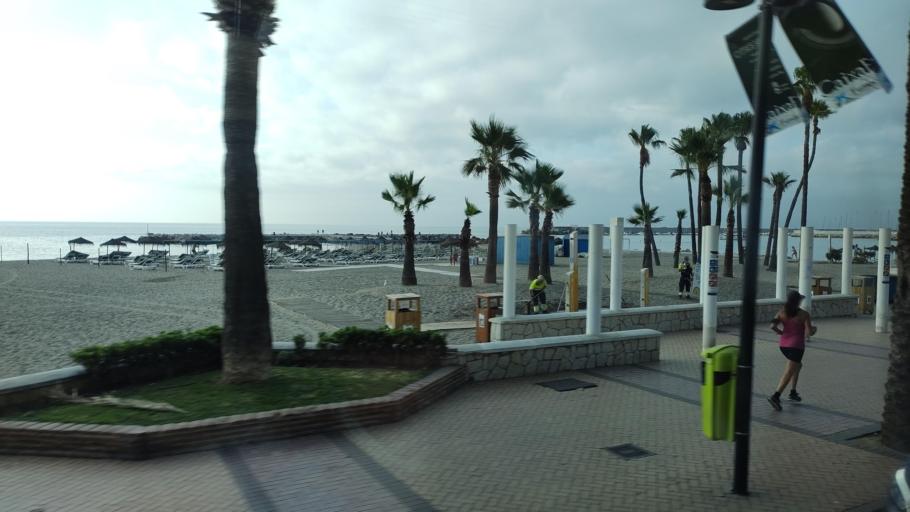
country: ES
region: Andalusia
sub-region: Provincia de Malaga
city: Fuengirola
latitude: 36.5470
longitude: -4.6164
